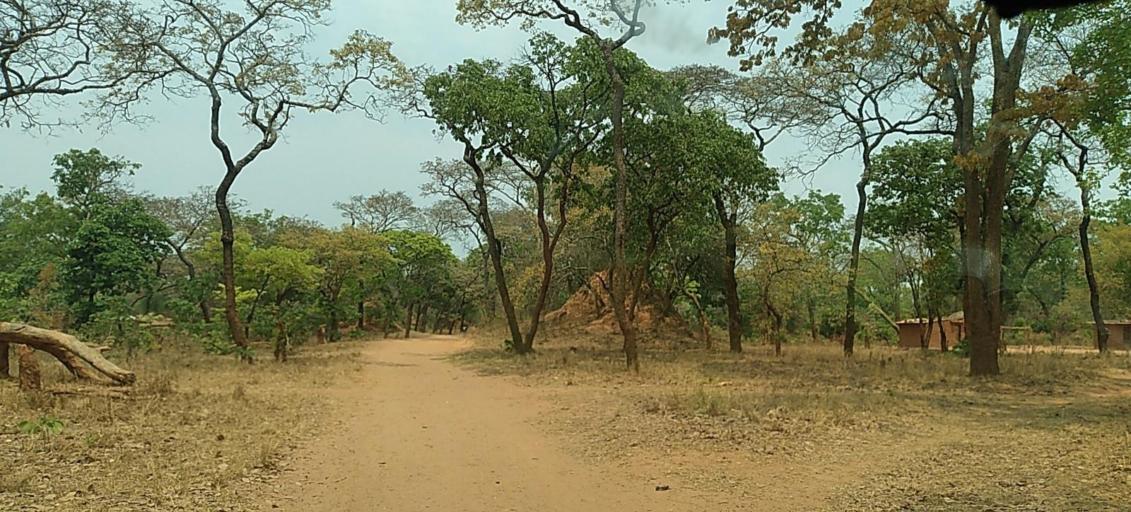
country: ZM
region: North-Western
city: Kabompo
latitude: -13.5746
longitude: 24.4387
